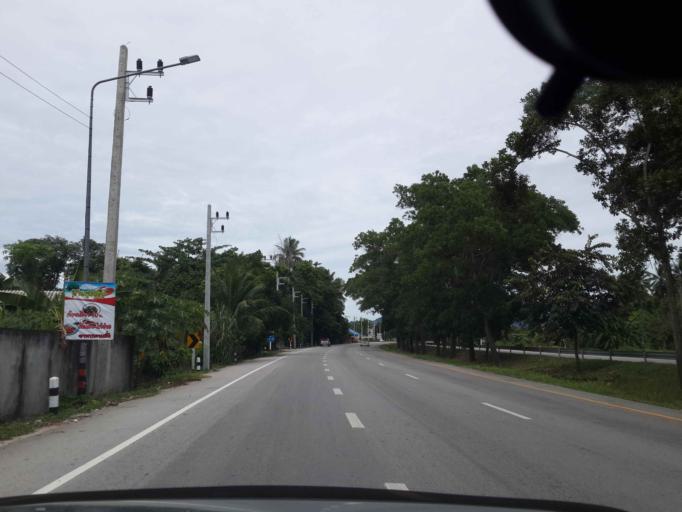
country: TH
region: Narathiwat
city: Yi-ngo
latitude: 6.4038
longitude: 101.7179
